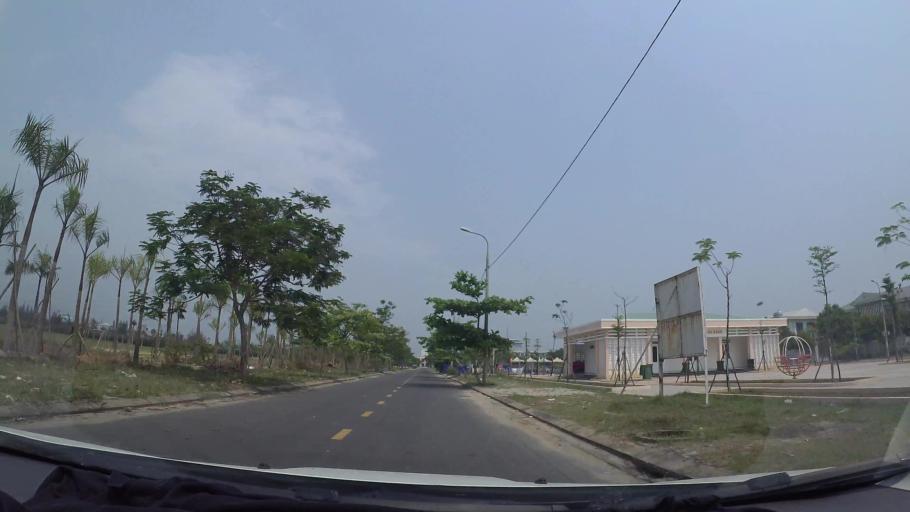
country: VN
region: Da Nang
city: Cam Le
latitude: 15.9948
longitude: 108.2105
